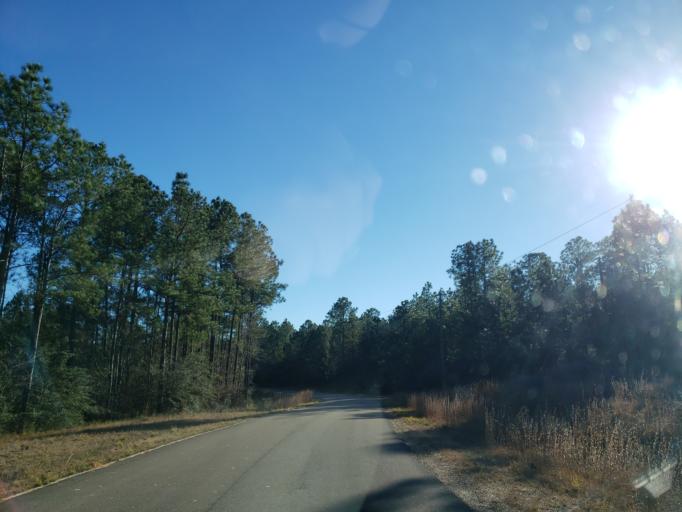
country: US
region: Mississippi
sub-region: Lamar County
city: Sumrall
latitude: 31.3581
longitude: -89.4760
